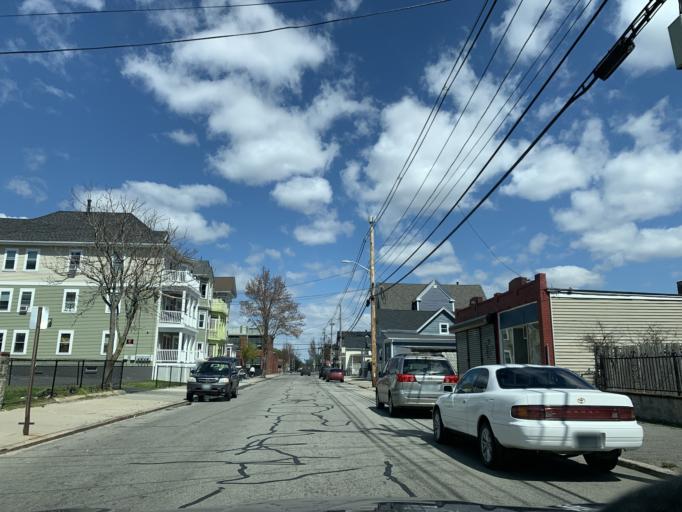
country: US
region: Rhode Island
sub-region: Providence County
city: Providence
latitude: 41.8031
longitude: -71.4137
